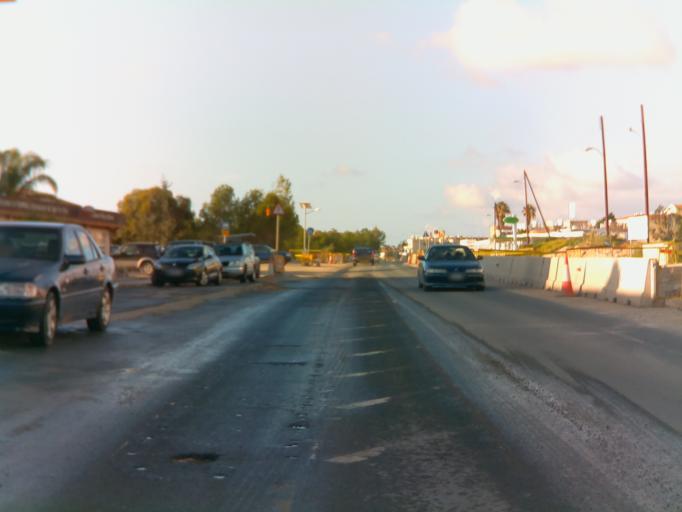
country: CY
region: Pafos
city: Paphos
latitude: 34.7723
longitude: 32.4097
